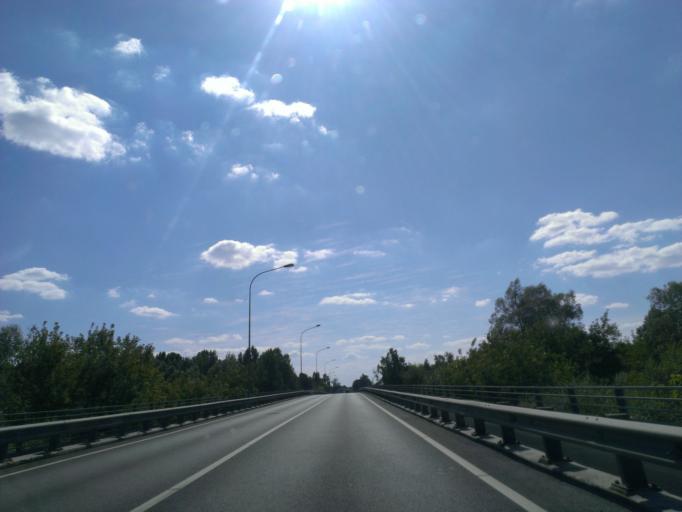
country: LV
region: Adazi
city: Adazi
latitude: 57.1209
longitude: 24.3256
